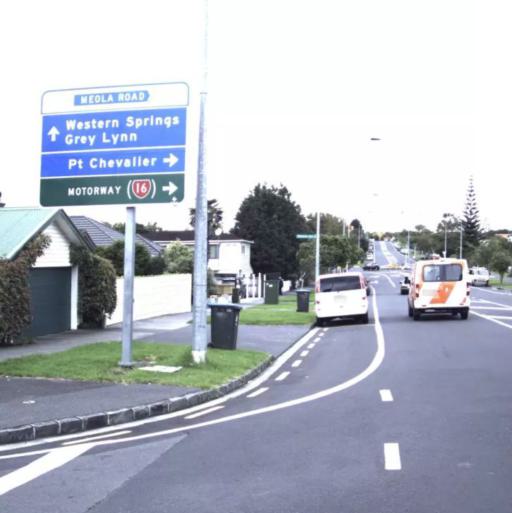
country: NZ
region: Auckland
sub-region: Auckland
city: Auckland
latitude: -36.8545
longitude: 174.7188
